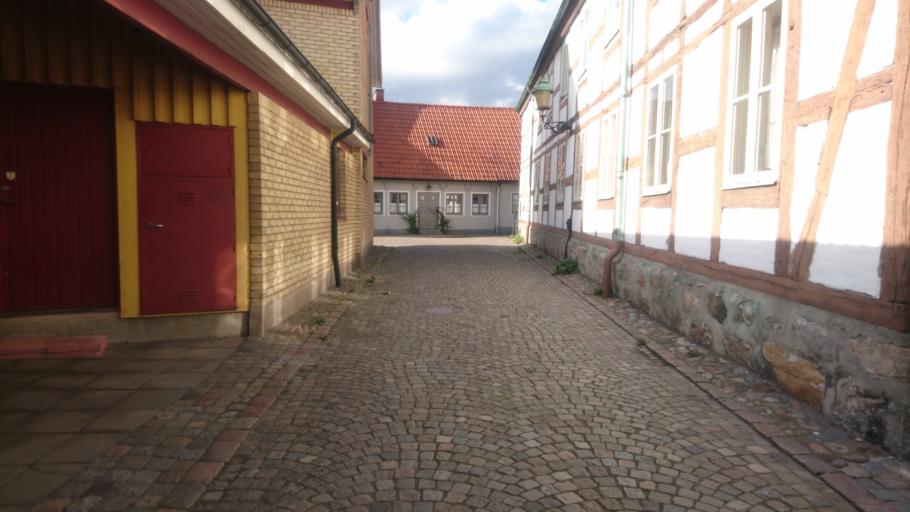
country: SE
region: Skane
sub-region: Ystads Kommun
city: Ystad
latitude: 55.4284
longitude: 13.8232
